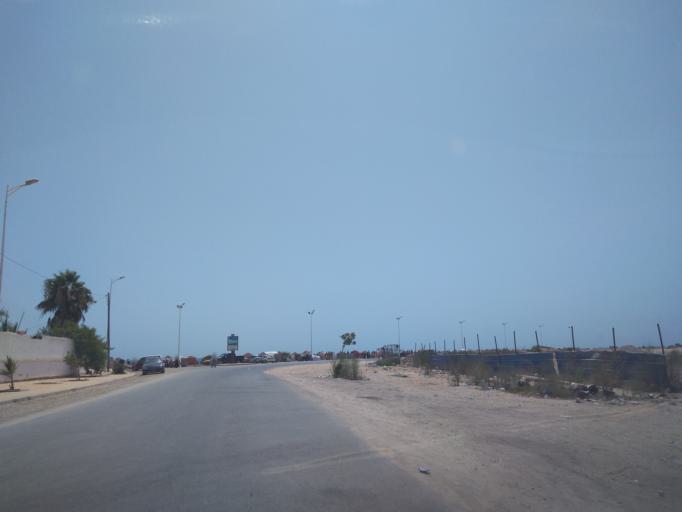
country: TN
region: Safaqis
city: Al Qarmadah
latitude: 34.7279
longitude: 10.7811
